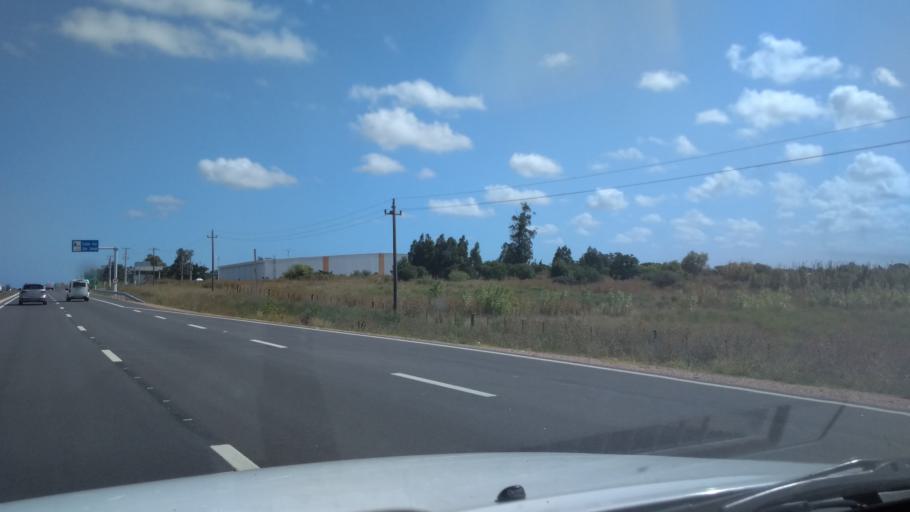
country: UY
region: Canelones
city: Colonia Nicolich
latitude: -34.8085
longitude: -56.0060
